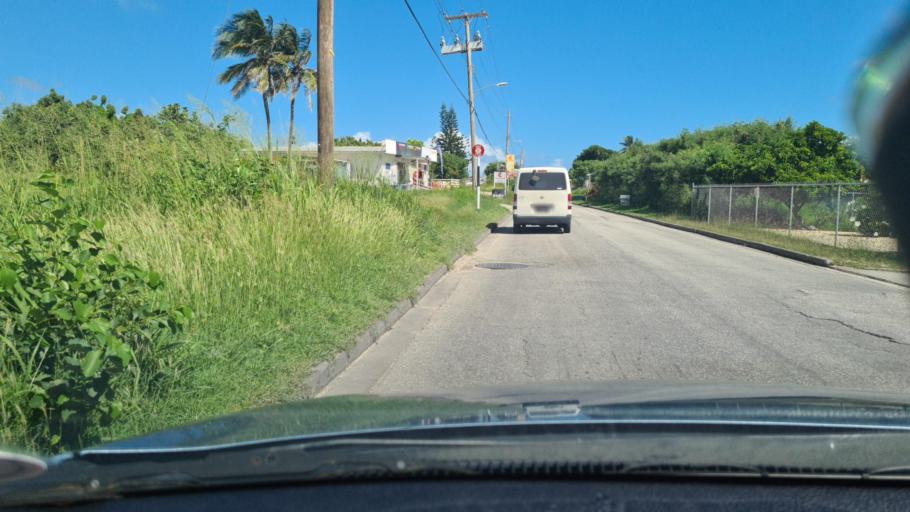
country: BB
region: Saint Philip
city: Crane
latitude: 13.1245
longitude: -59.4502
